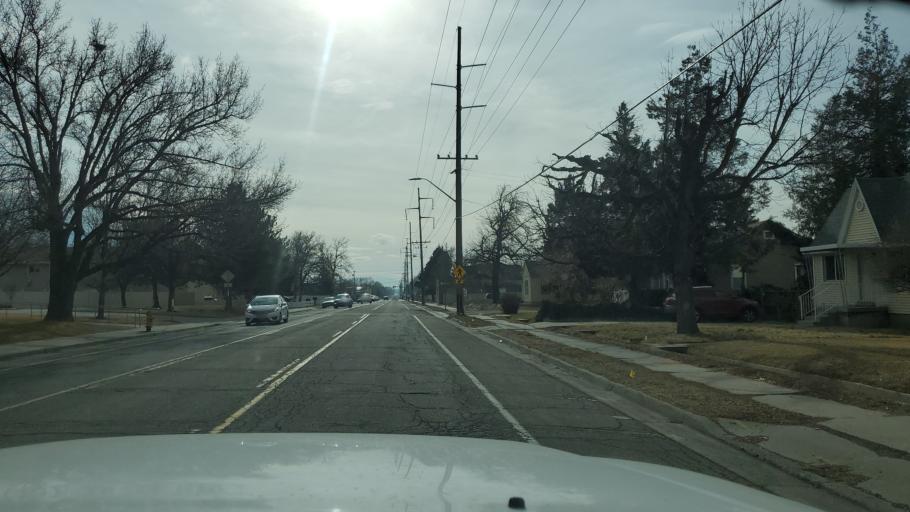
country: US
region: Utah
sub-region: Salt Lake County
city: Millcreek
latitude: 40.7028
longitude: -111.8655
